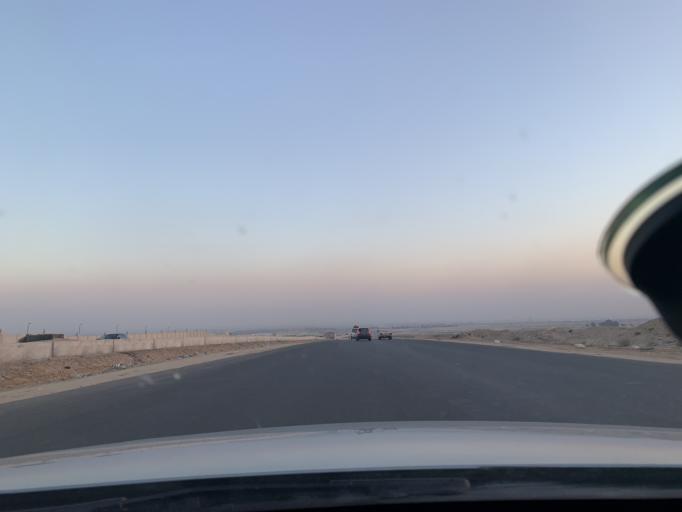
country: EG
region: Muhafazat al Qalyubiyah
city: Al Khankah
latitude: 30.2280
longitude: 31.4277
